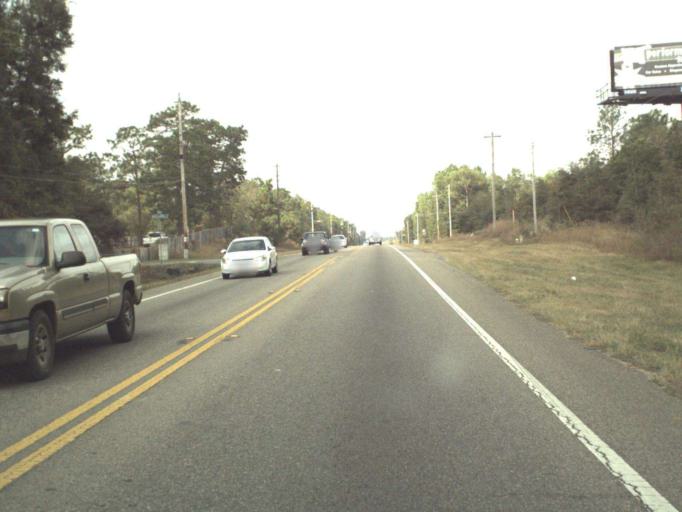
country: US
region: Florida
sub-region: Leon County
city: Tallahassee
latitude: 30.3822
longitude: -84.3060
